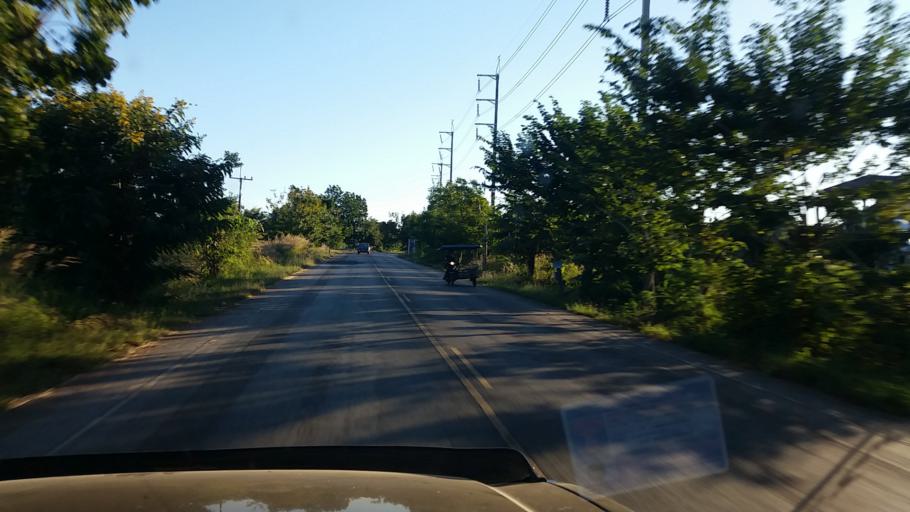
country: TH
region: Chaiyaphum
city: Nong Bua Rawe
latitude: 15.7083
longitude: 101.7382
